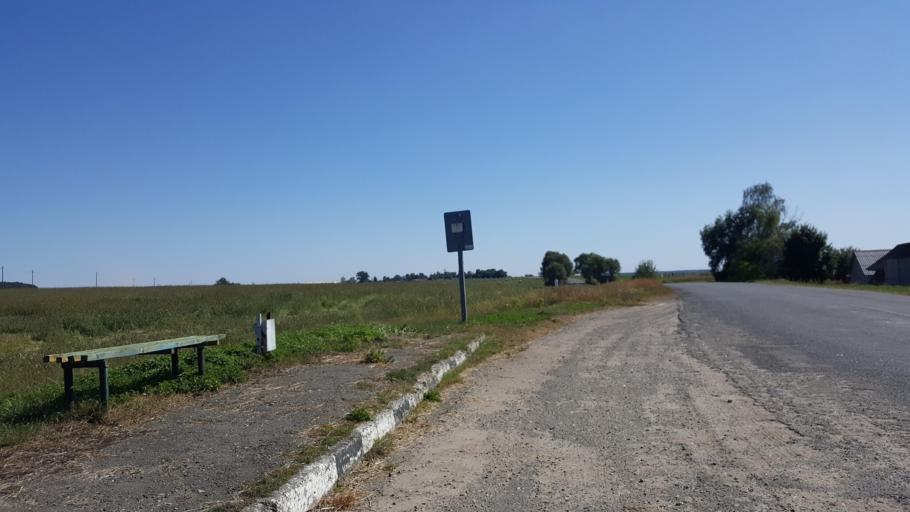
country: PL
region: Lublin Voivodeship
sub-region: Powiat bialski
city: Terespol
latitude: 52.2113
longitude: 23.5239
